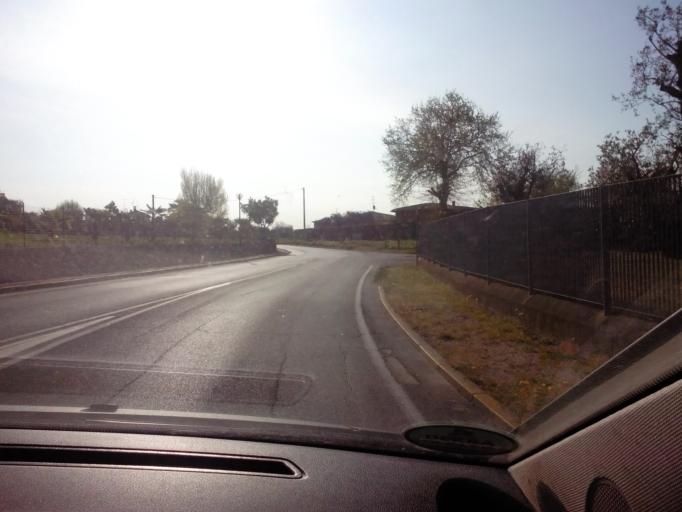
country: IT
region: Lombardy
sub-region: Provincia di Brescia
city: Manerba del Garda
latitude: 45.5476
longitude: 10.5405
